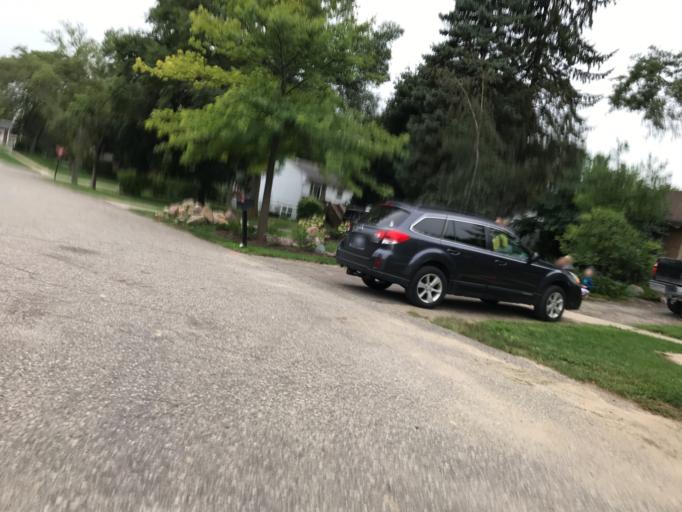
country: US
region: Michigan
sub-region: Oakland County
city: South Lyon
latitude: 42.4647
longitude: -83.6423
